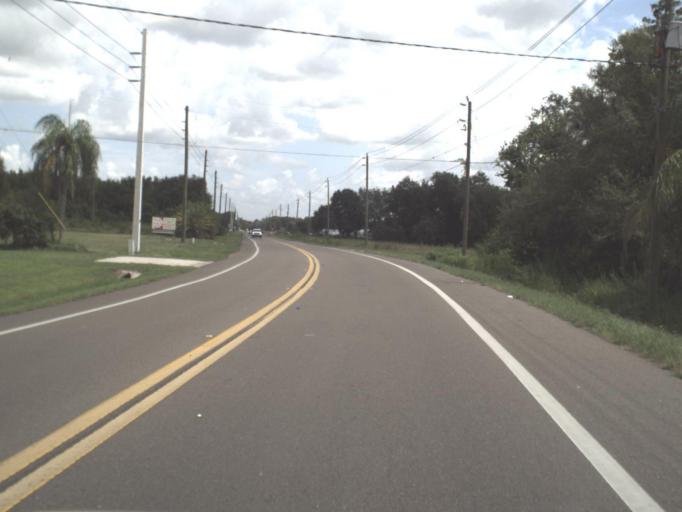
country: US
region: Florida
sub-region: DeSoto County
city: Southeast Arcadia
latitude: 27.1927
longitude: -81.8671
